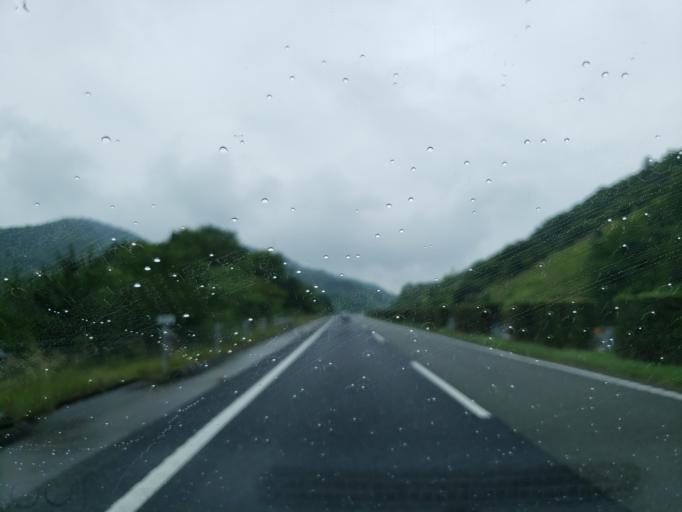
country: JP
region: Hyogo
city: Fukura
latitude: 34.2828
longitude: 134.7099
